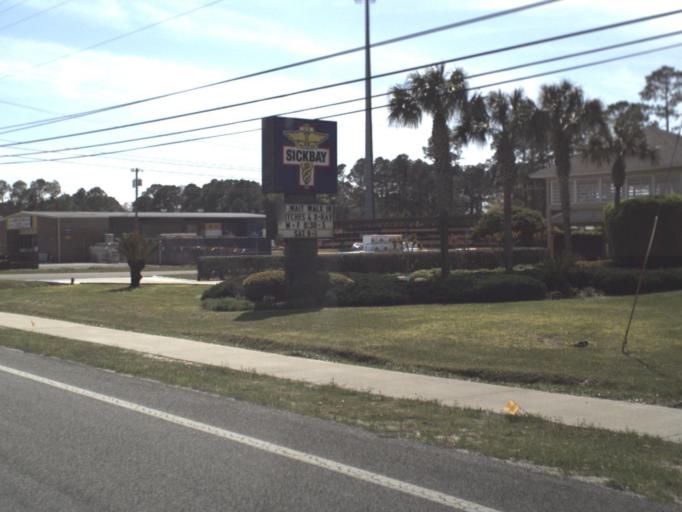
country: US
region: Florida
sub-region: Bay County
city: Hiland Park
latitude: 30.2101
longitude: -85.6497
